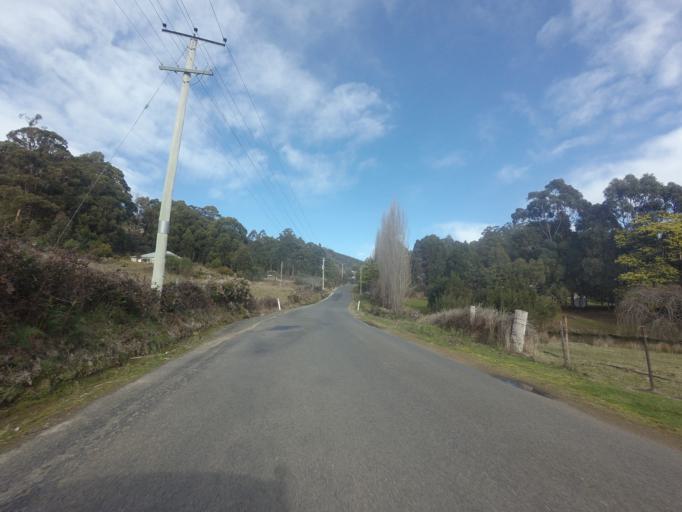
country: AU
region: Tasmania
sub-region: Kingborough
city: Margate
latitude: -42.9958
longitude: 147.1813
